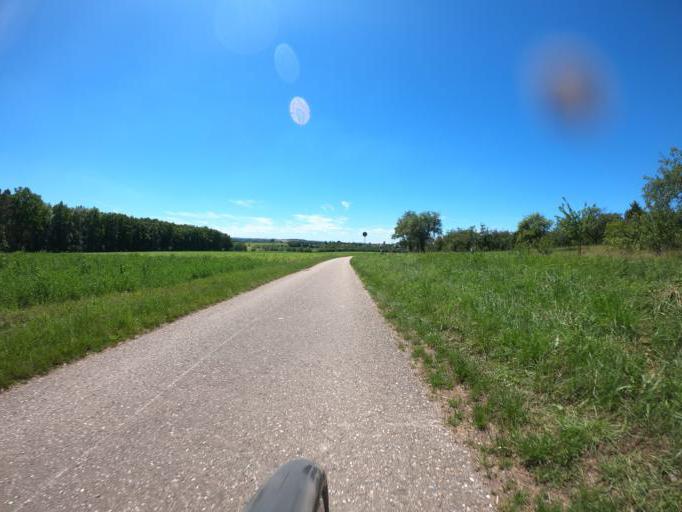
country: DE
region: Baden-Wuerttemberg
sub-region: Regierungsbezirk Stuttgart
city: Vaihingen an der Enz
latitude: 48.9695
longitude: 8.9648
